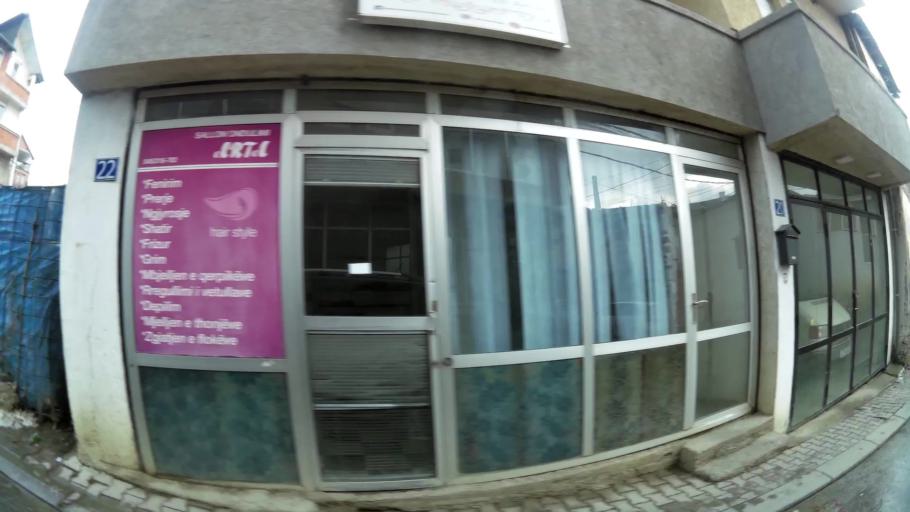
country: XK
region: Pristina
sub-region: Komuna e Prishtines
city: Pristina
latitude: 42.6721
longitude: 21.1614
